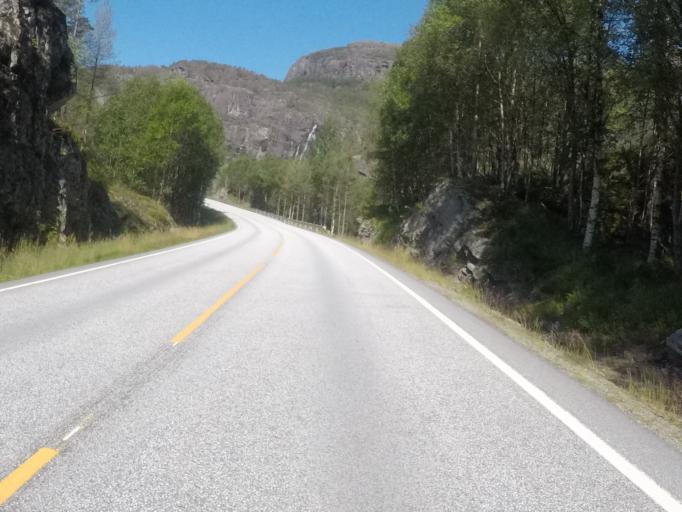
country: NO
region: Sogn og Fjordane
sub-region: Bremanger
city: Svelgen
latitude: 61.6406
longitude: 5.2953
